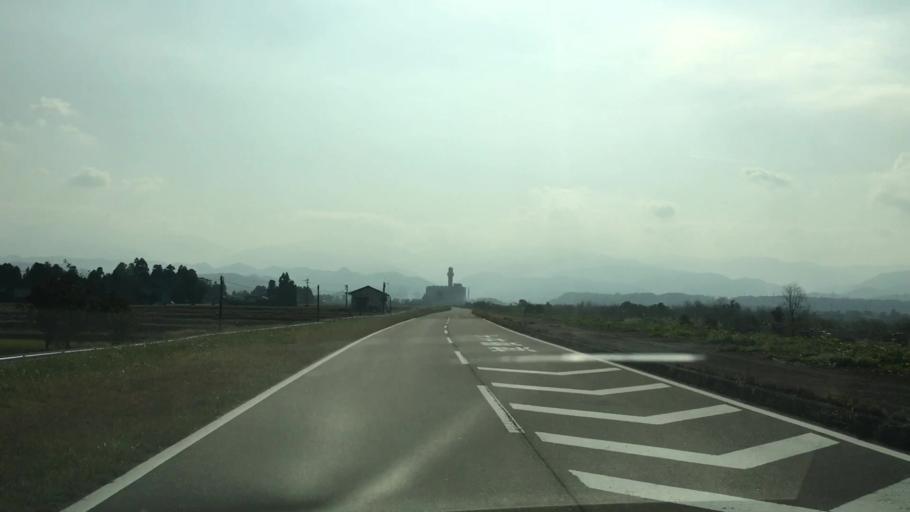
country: JP
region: Toyama
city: Toyama-shi
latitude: 36.6386
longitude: 137.2899
